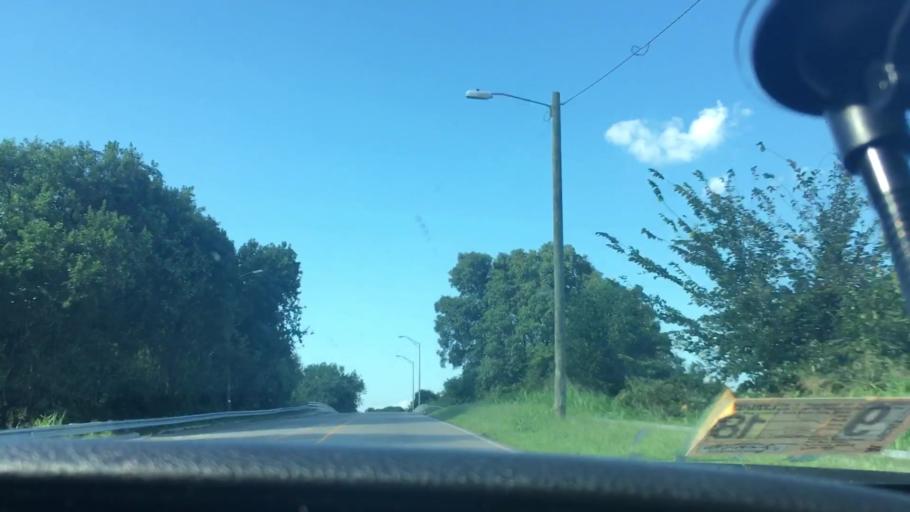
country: US
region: Virginia
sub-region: City of Chesapeake
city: Chesapeake
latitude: 36.8010
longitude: -76.2763
